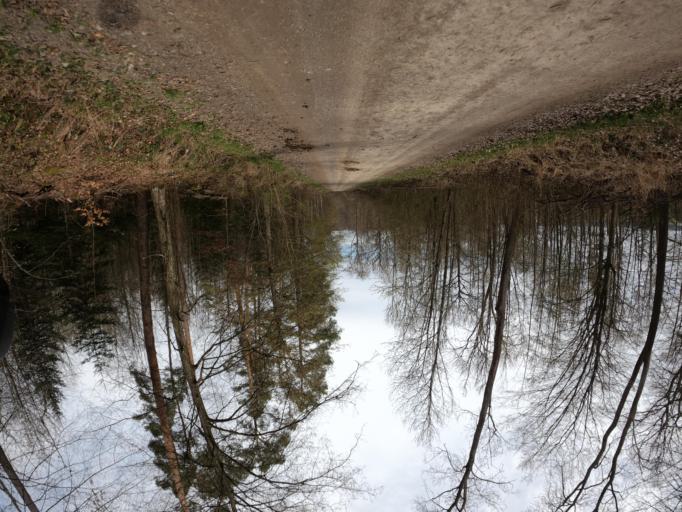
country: DE
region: Baden-Wuerttemberg
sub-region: Regierungsbezirk Stuttgart
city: Waldenbuch
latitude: 48.6281
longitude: 9.1667
